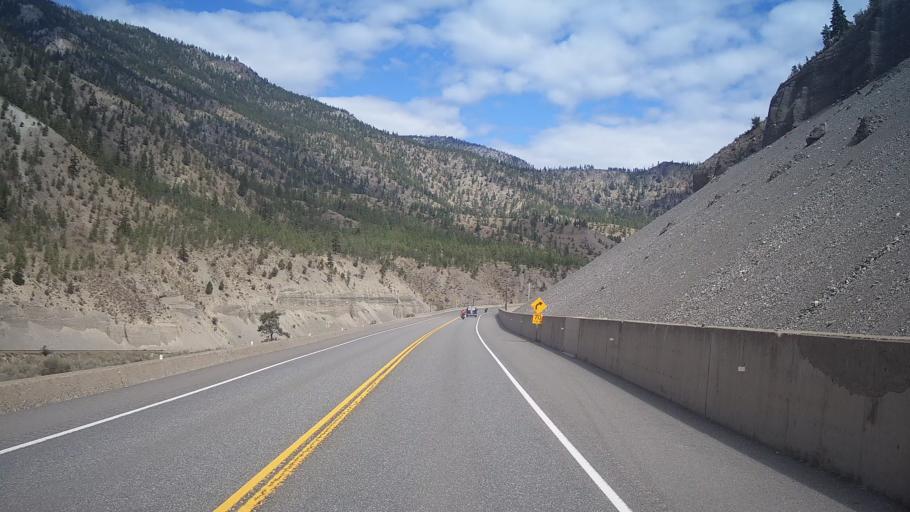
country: CA
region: British Columbia
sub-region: Thompson-Nicola Regional District
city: Ashcroft
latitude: 50.2775
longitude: -121.4051
